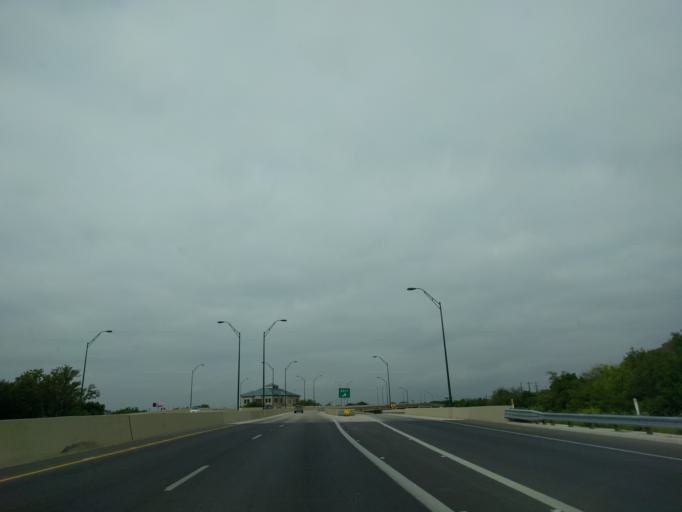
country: US
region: Texas
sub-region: Bexar County
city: Castle Hills
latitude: 29.5540
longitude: -98.4817
